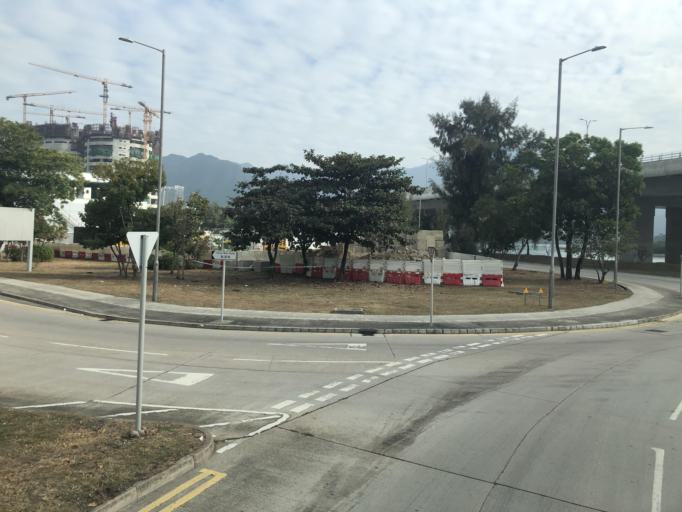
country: HK
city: Tai O
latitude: 22.2945
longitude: 113.9218
